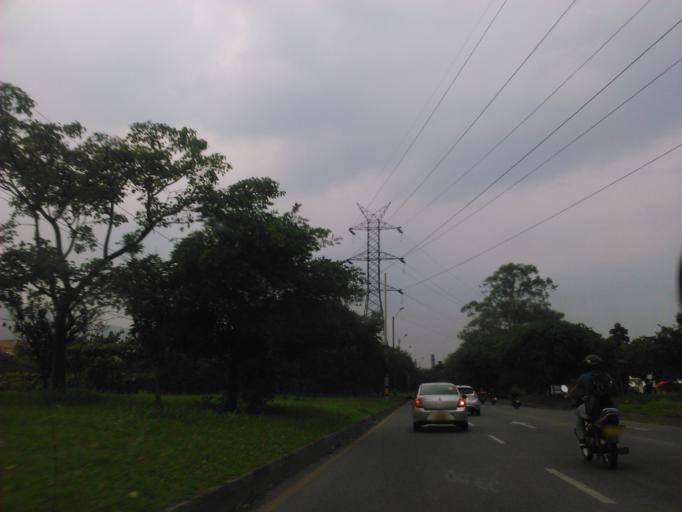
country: CO
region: Antioquia
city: Envigado
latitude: 6.1674
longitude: -75.6025
